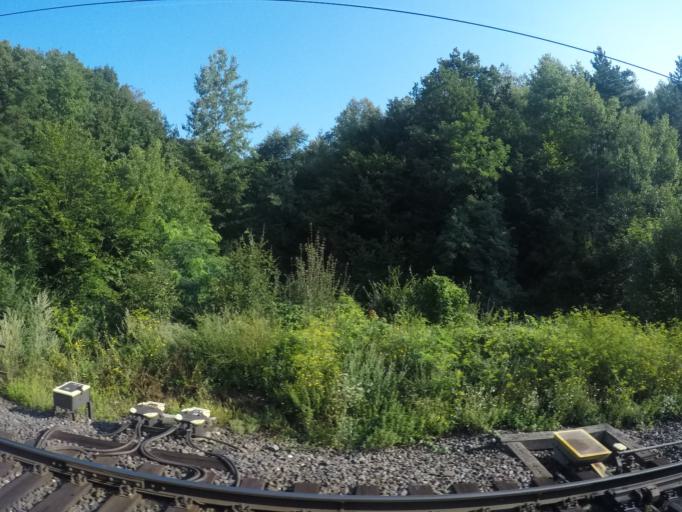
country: SK
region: Kosicky
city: Gelnica
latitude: 48.8735
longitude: 21.1003
